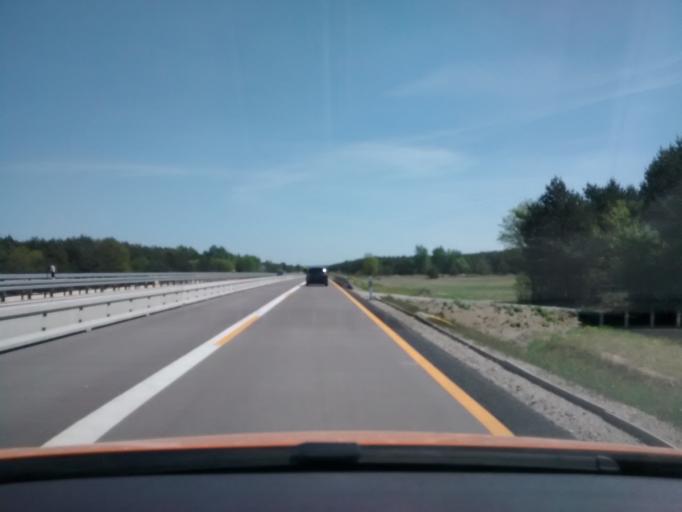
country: DE
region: Brandenburg
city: Spreenhagen
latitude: 52.3106
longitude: 13.8337
